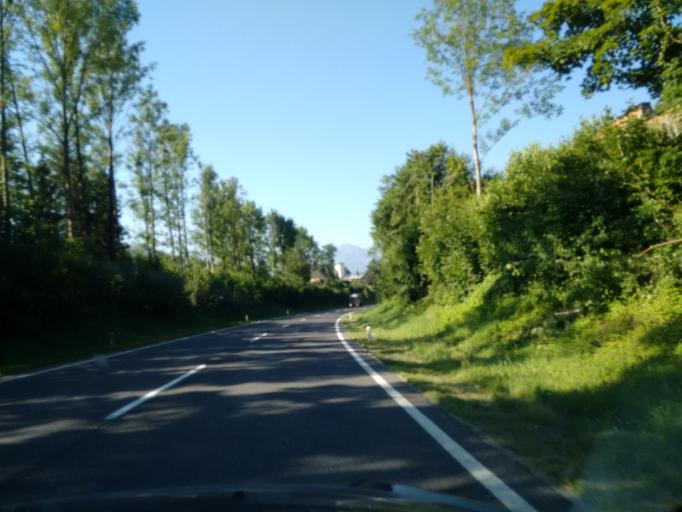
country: AT
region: Upper Austria
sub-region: Politischer Bezirk Gmunden
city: Bad Ischl
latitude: 47.7070
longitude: 13.6287
